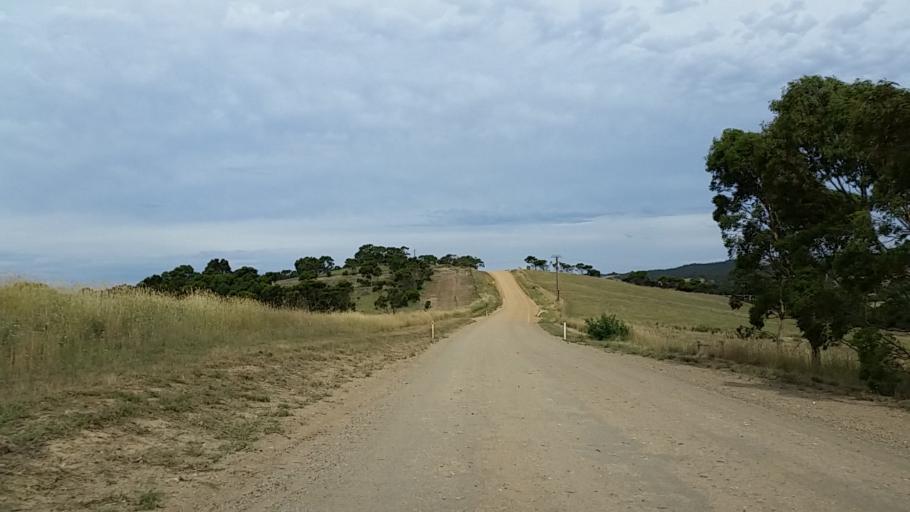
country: AU
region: South Australia
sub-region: Yankalilla
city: Normanville
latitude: -35.4111
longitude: 138.4132
